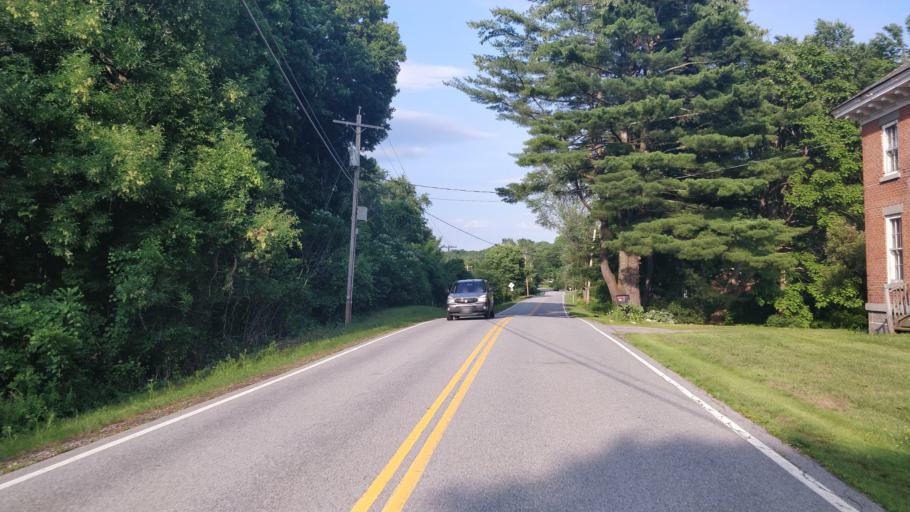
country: US
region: New York
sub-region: Saratoga County
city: North Ballston Spa
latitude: 43.0238
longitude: -73.8051
